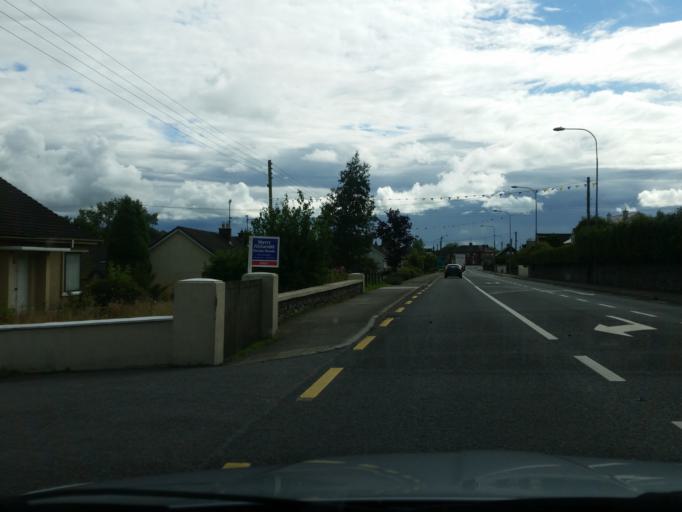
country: IE
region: Ulster
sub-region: An Cabhan
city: Cavan
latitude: 54.0471
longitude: -7.3762
